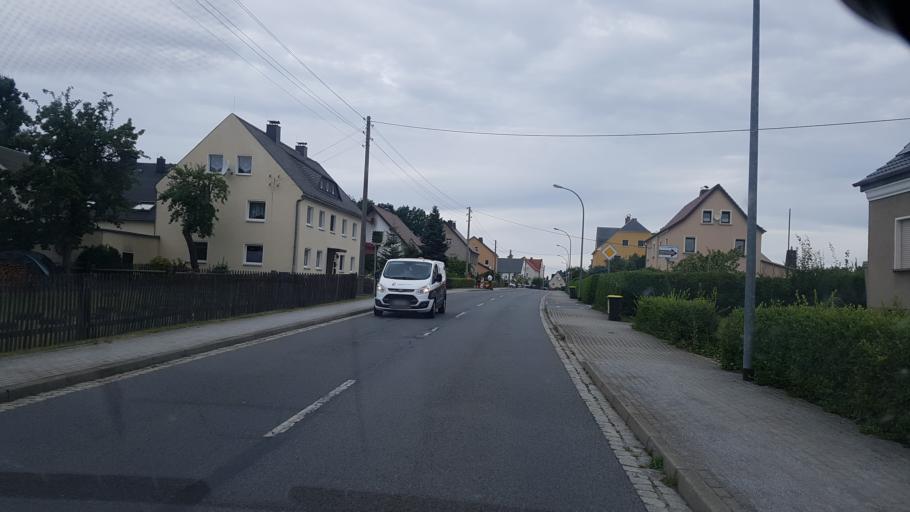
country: DE
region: Saxony
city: Ohorn
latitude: 51.1684
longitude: 14.0466
